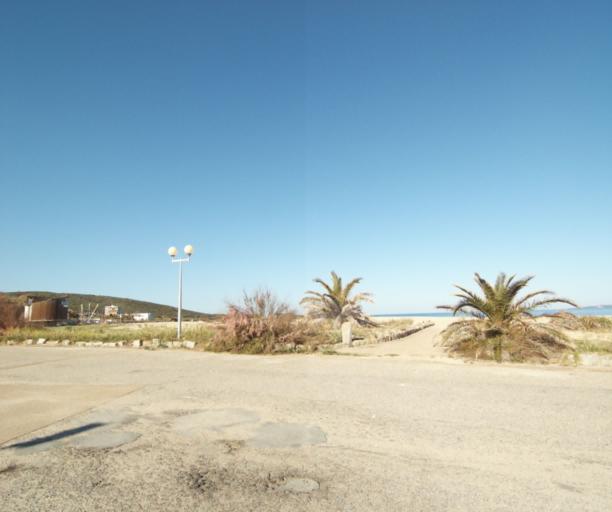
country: FR
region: Corsica
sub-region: Departement de la Corse-du-Sud
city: Propriano
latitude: 41.6766
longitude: 8.8974
